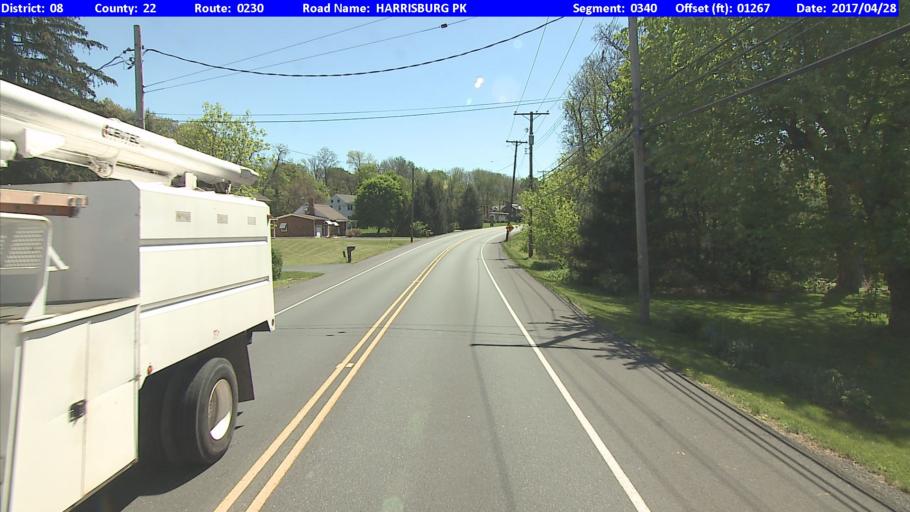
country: US
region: Pennsylvania
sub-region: Dauphin County
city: Middletown
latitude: 40.1897
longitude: -76.6824
